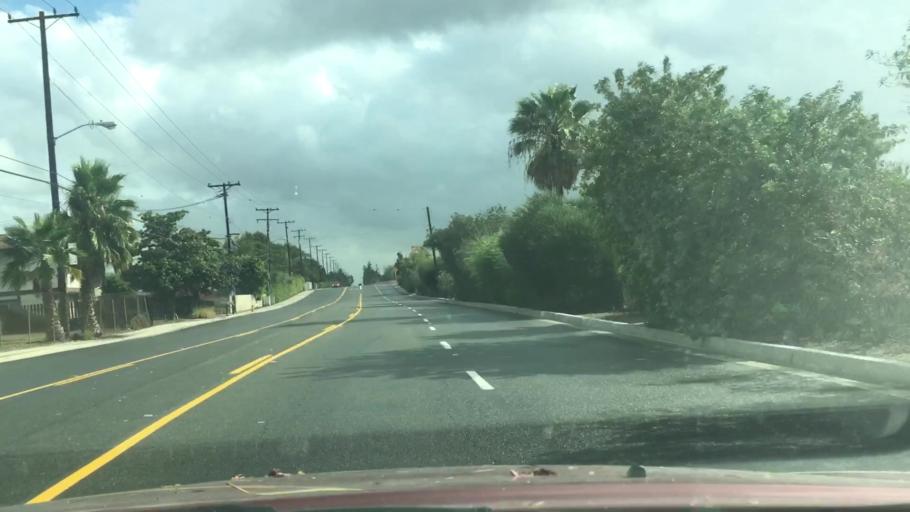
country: US
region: California
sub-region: Los Angeles County
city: La Mirada
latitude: 33.8931
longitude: -118.0208
